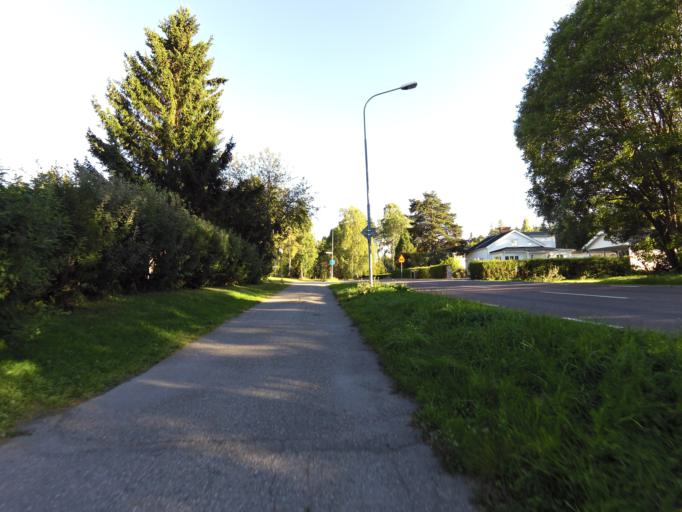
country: SE
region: Gaevleborg
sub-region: Gavle Kommun
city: Gavle
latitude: 60.7103
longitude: 17.1472
